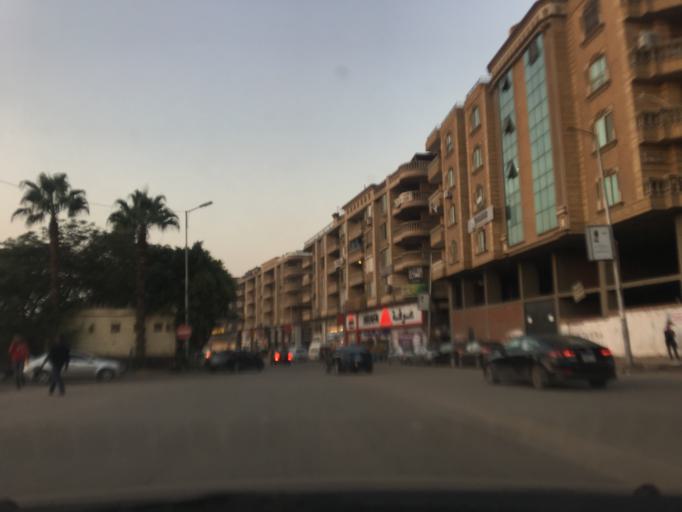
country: EG
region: Al Jizah
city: Al Jizah
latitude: 29.9872
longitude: 31.1411
